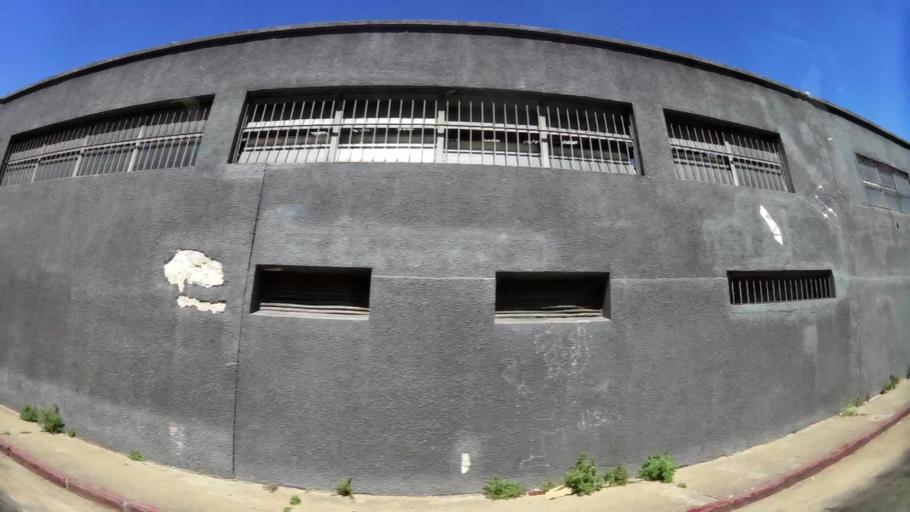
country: UY
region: Montevideo
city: Montevideo
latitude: -34.9022
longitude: -56.2017
